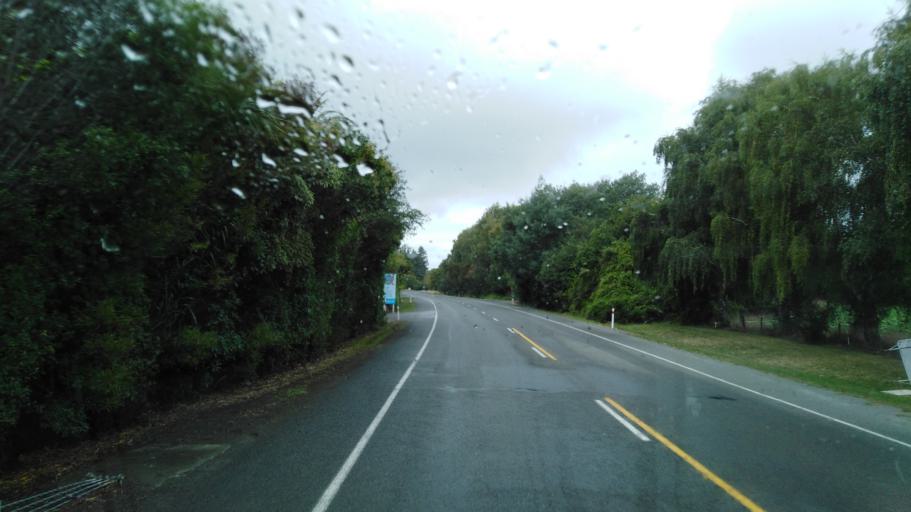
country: NZ
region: Marlborough
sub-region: Marlborough District
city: Blenheim
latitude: -41.4577
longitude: 173.9538
